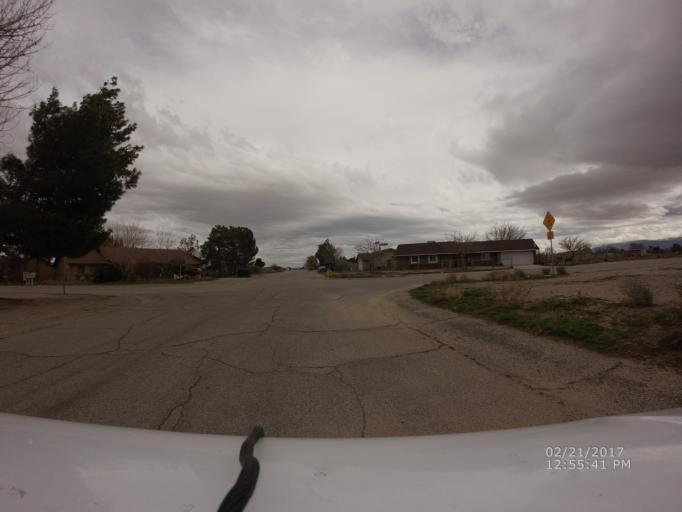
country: US
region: California
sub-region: Los Angeles County
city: Lake Los Angeles
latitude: 34.6398
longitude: -117.8497
